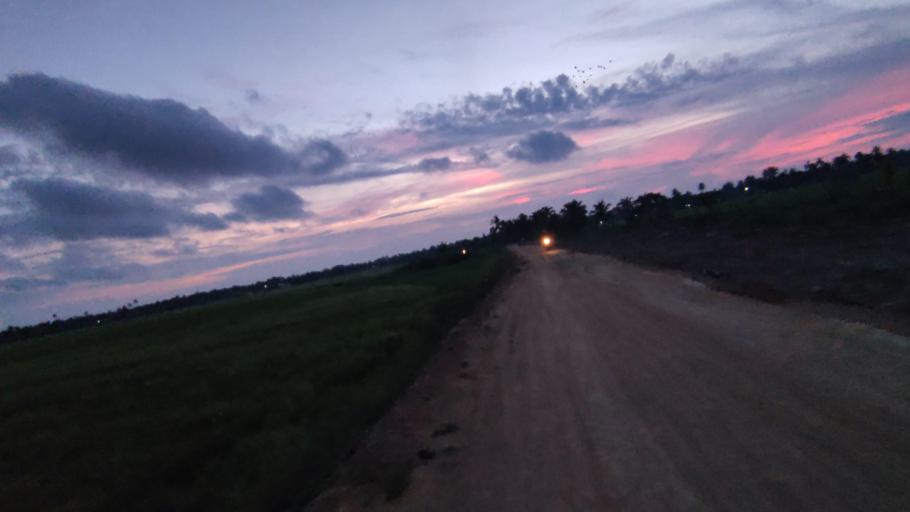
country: IN
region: Kerala
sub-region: Alappuzha
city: Shertallai
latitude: 9.6430
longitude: 76.4365
